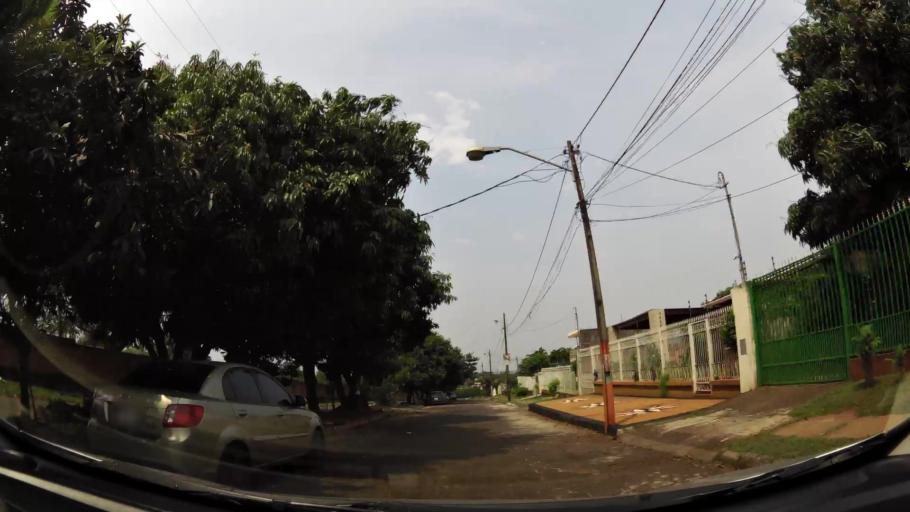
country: PY
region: Alto Parana
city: Presidente Franco
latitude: -25.5384
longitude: -54.6284
